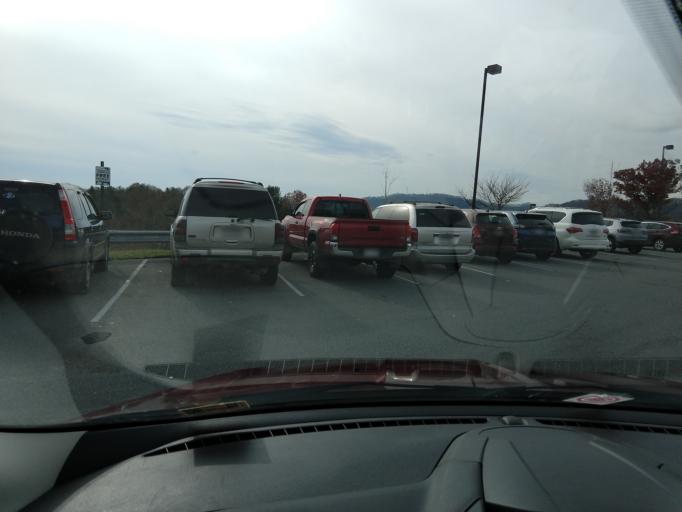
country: US
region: West Virginia
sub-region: Nicholas County
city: Summersville
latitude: 38.2924
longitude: -80.8307
